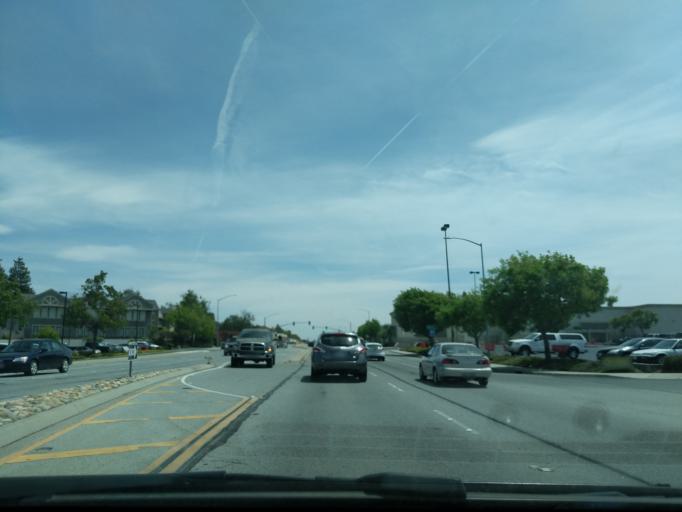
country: US
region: California
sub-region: San Benito County
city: Hollister
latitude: 36.8367
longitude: -121.3893
